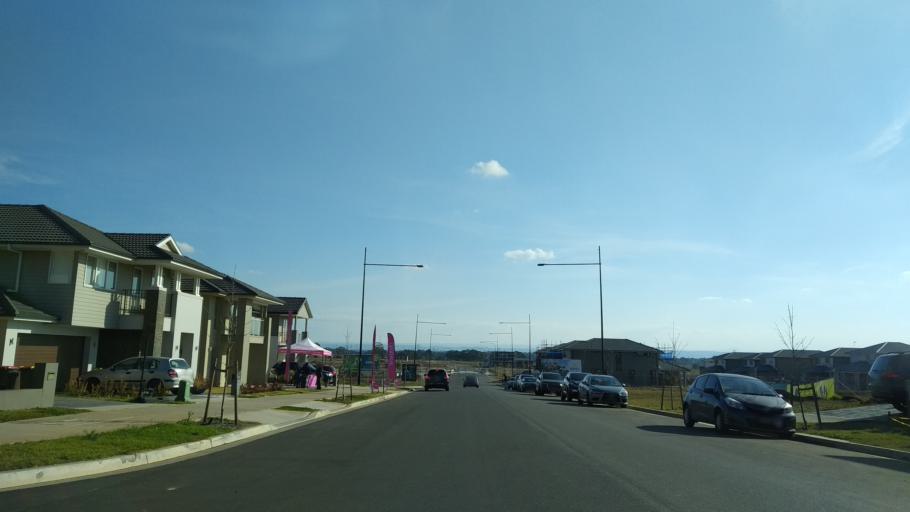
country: AU
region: New South Wales
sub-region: Blacktown
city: Blackett
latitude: -33.6959
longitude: 150.8089
